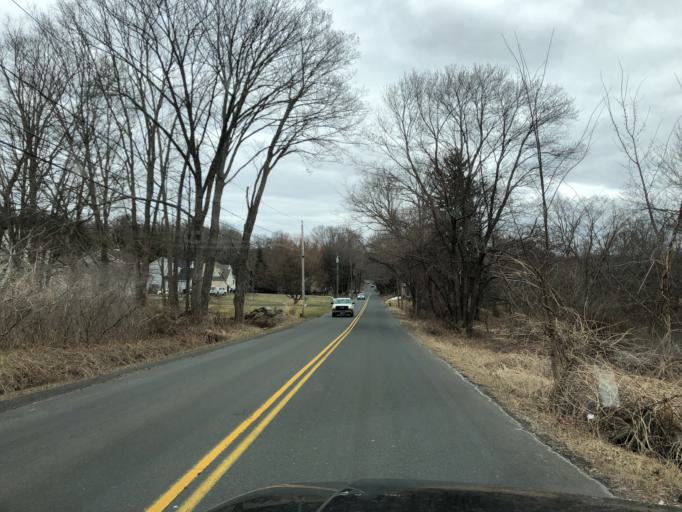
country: US
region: Connecticut
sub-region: Hartford County
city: Plainville
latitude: 41.6291
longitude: -72.8906
